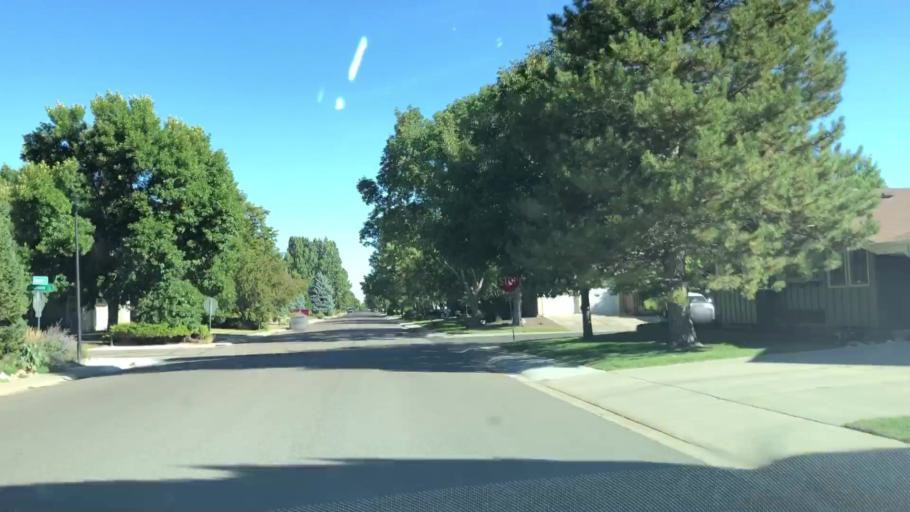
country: US
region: Colorado
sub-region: Larimer County
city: Fort Collins
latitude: 40.5548
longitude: -105.0492
